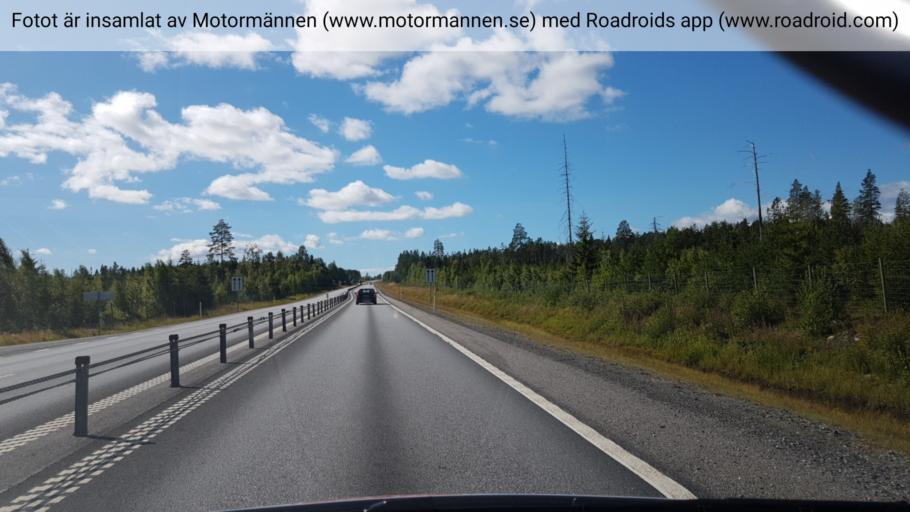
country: SE
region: Vaesterbotten
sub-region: Umea Kommun
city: Hoernefors
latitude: 63.6637
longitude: 19.9653
